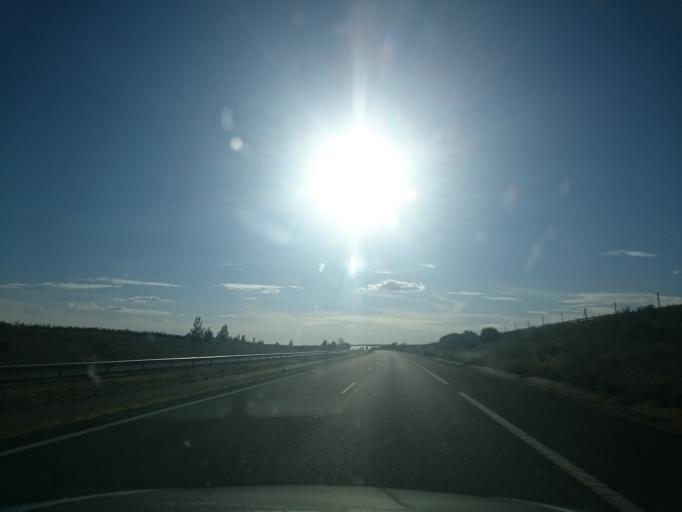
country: ES
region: Castille and Leon
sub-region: Provincia de Burgos
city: Villasandino
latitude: 42.3980
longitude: -4.1208
